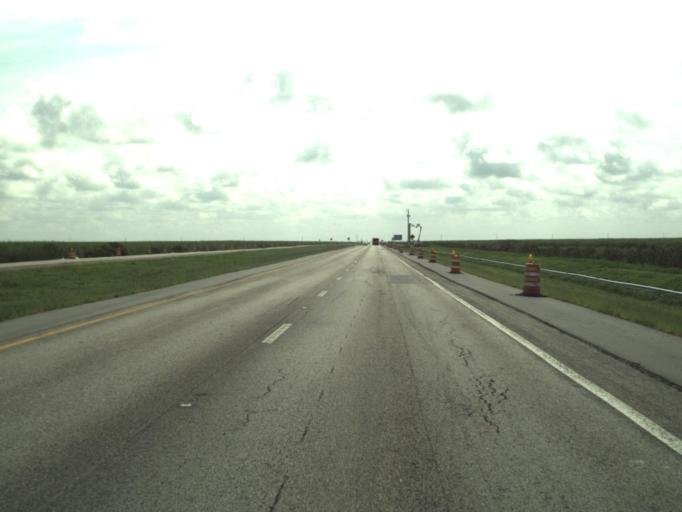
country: US
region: Florida
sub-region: Palm Beach County
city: Belle Glade
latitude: 26.7259
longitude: -80.5830
